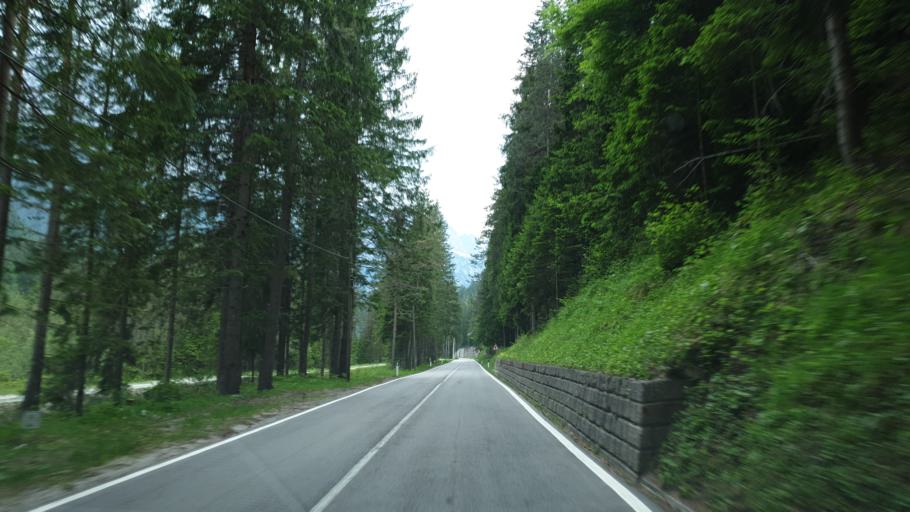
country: IT
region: Veneto
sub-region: Provincia di Belluno
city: Auronzo
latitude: 46.5640
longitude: 12.3462
